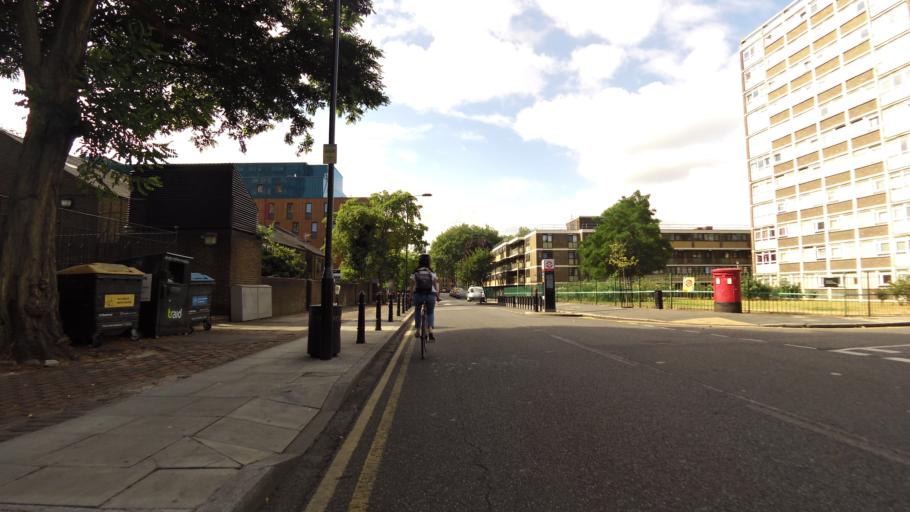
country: GB
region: England
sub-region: Greater London
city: Barbican
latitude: 51.5324
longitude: -0.0831
